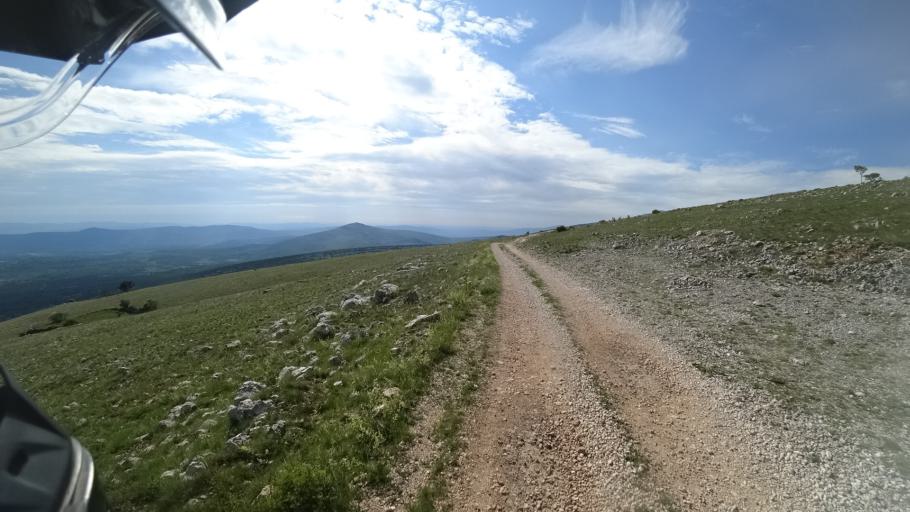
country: HR
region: Splitsko-Dalmatinska
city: Hrvace
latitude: 43.7726
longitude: 16.4604
